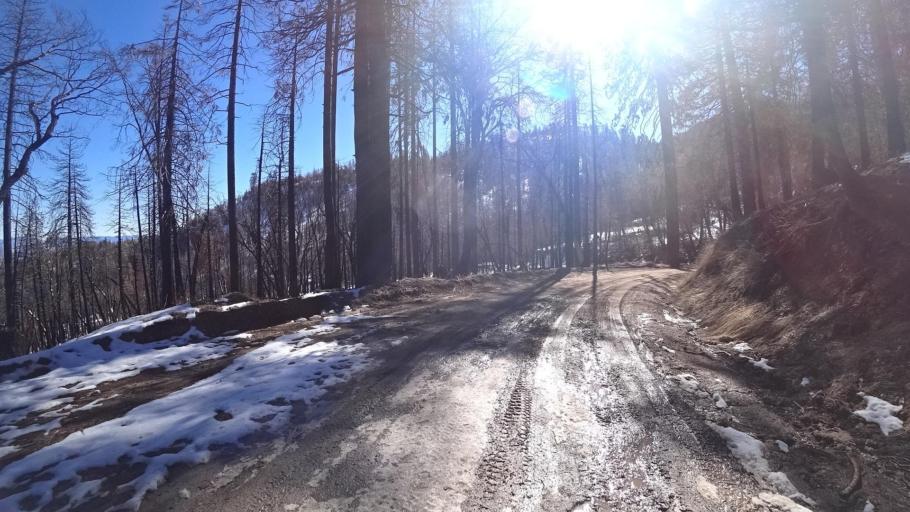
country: US
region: California
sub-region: Kern County
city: Alta Sierra
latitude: 35.7178
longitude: -118.5444
